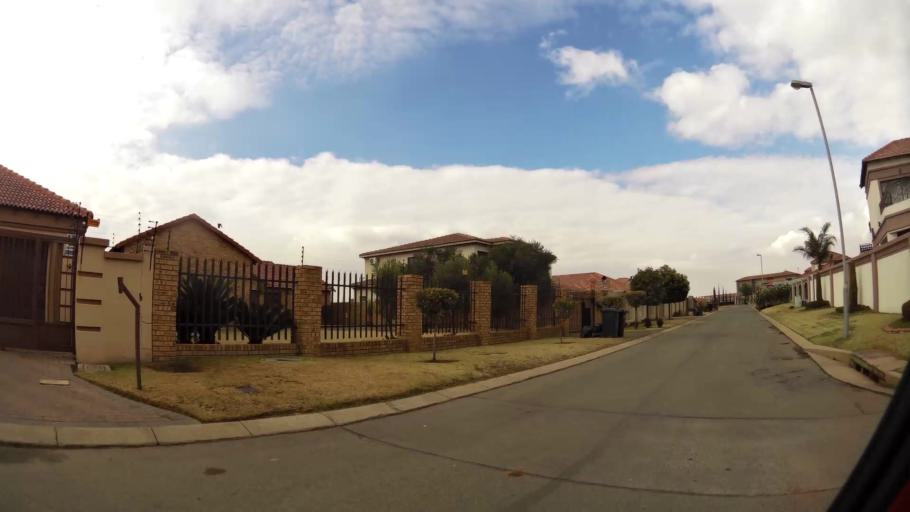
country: ZA
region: Gauteng
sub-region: Sedibeng District Municipality
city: Vanderbijlpark
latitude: -26.7273
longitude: 27.8699
